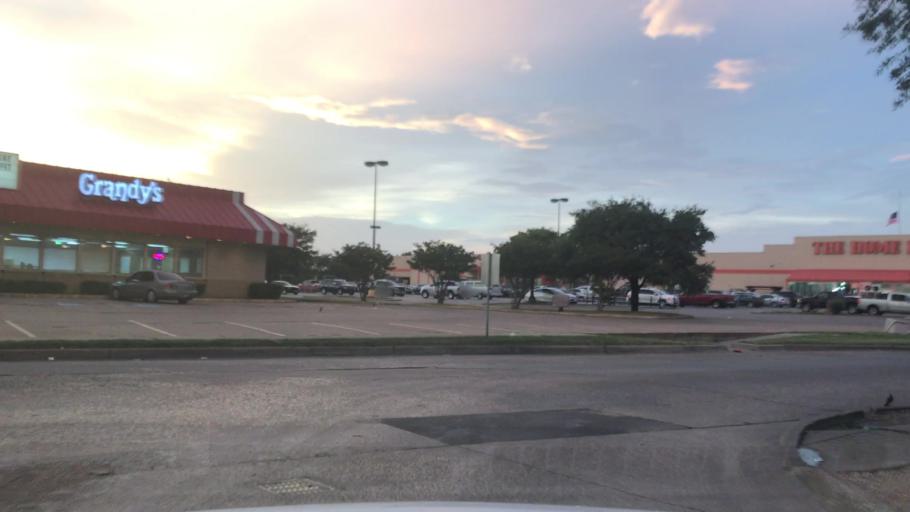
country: US
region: Texas
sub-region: Dallas County
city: Balch Springs
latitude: 32.7196
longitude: -96.6180
